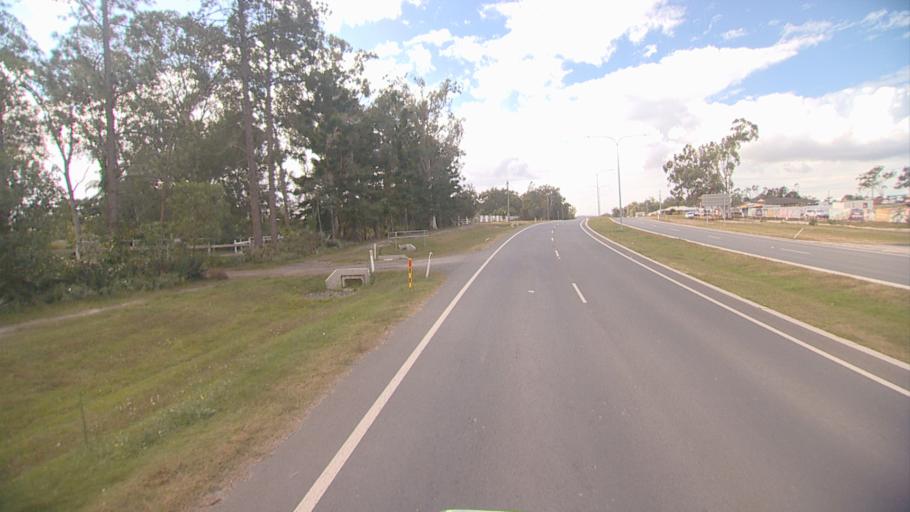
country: AU
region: Queensland
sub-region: Logan
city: Logan Reserve
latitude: -27.7065
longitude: 153.0942
